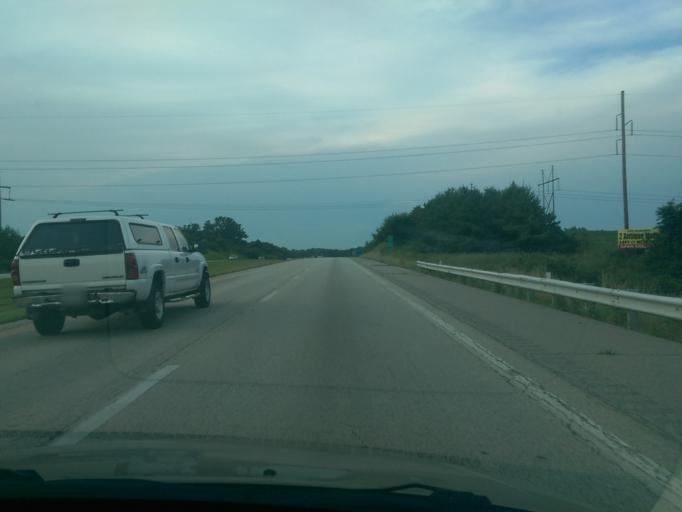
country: US
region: Missouri
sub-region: Andrew County
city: Country Club Village
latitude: 39.8425
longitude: -94.8051
